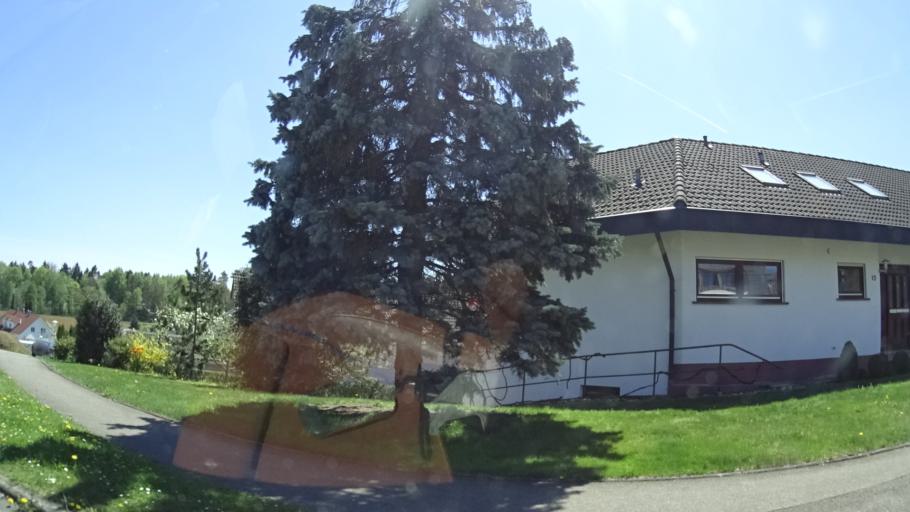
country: DE
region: Baden-Wuerttemberg
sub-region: Freiburg Region
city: Zimmern ob Rottweil
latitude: 48.1667
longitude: 8.5838
